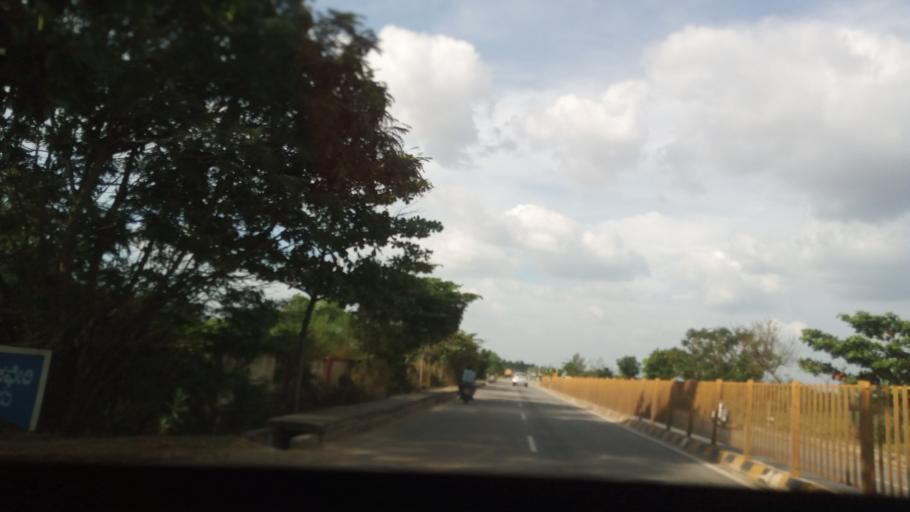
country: IN
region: Karnataka
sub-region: Mandya
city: Maddur
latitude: 12.6156
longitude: 77.0579
